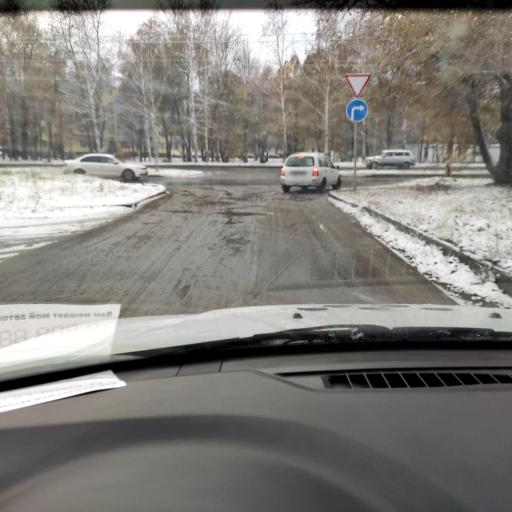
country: RU
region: Samara
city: Tol'yatti
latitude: 53.5140
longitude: 49.4486
